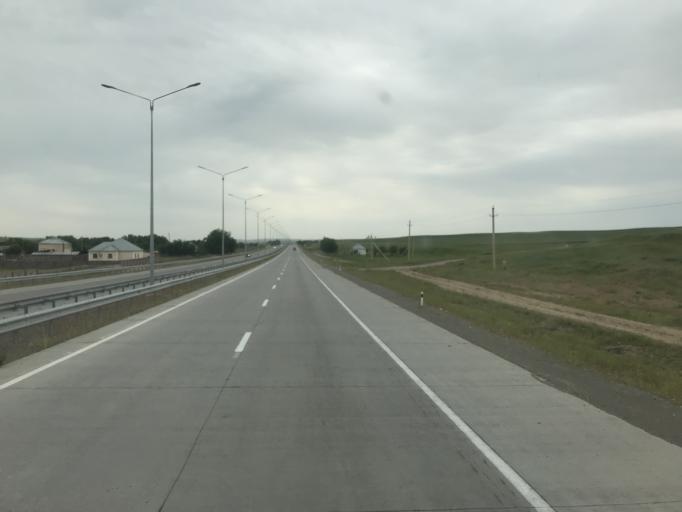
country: KZ
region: Ongtustik Qazaqstan
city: Qazyqurt
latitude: 41.8931
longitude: 69.4499
